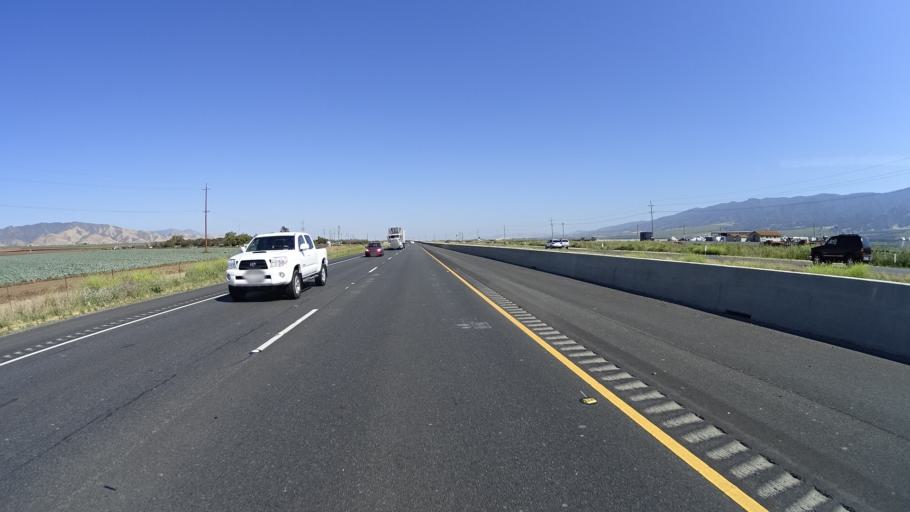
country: US
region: California
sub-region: Monterey County
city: Gonzales
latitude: 36.4860
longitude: -121.4201
